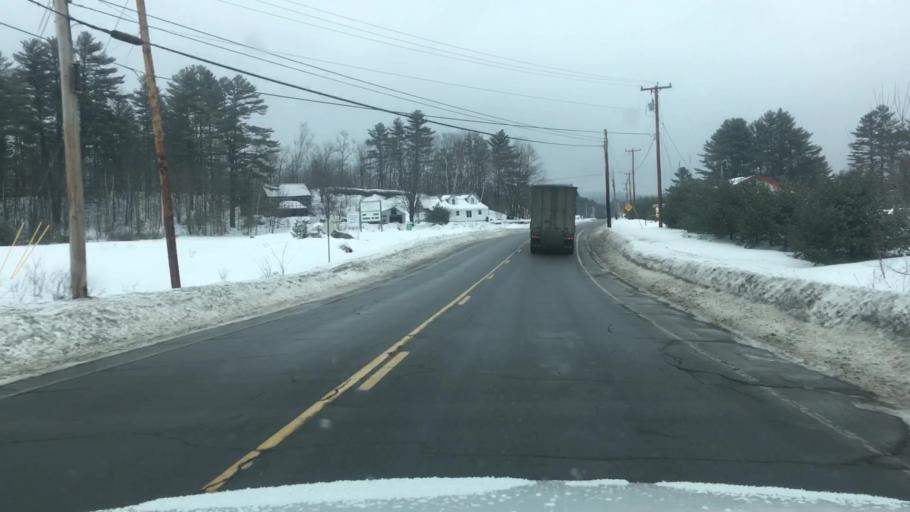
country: US
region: Maine
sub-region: Oxford County
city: Peru
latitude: 44.5188
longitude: -70.4173
